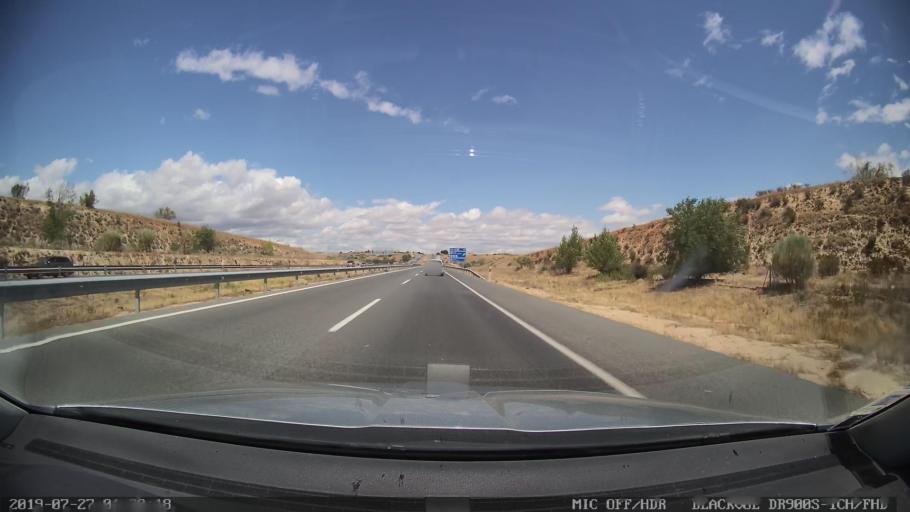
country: ES
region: Castille-La Mancha
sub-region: Province of Toledo
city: Valmojado
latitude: 40.1958
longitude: -4.1060
